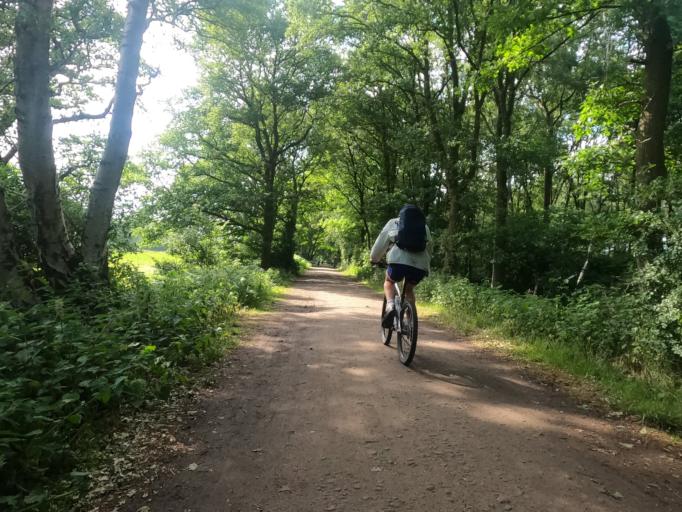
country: GB
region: England
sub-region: Cheshire West and Chester
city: Cuddington
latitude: 53.2121
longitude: -2.5920
